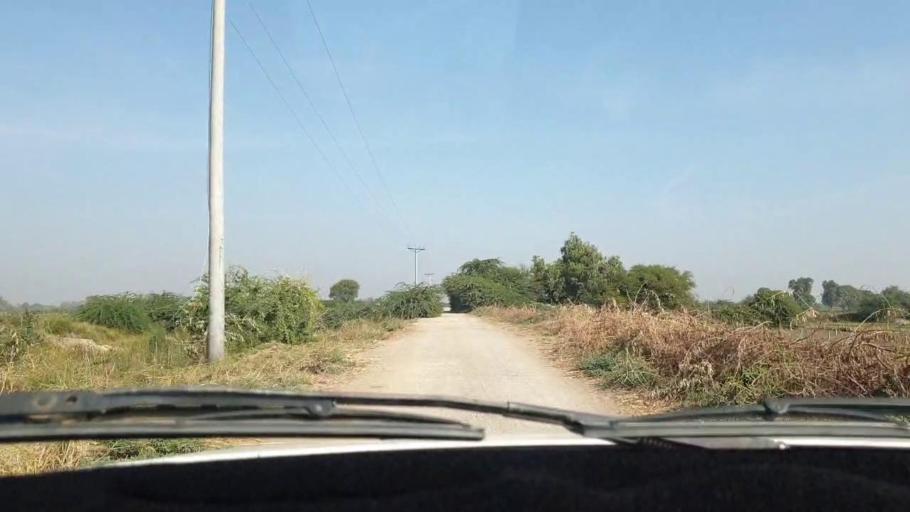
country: PK
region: Sindh
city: Bulri
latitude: 24.9685
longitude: 68.4559
